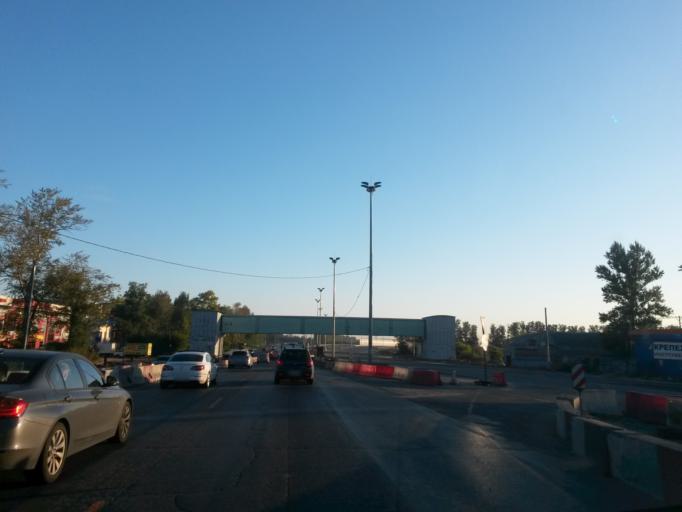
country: RU
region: Moskovskaya
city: Bolshevo
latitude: 55.9429
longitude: 37.8133
